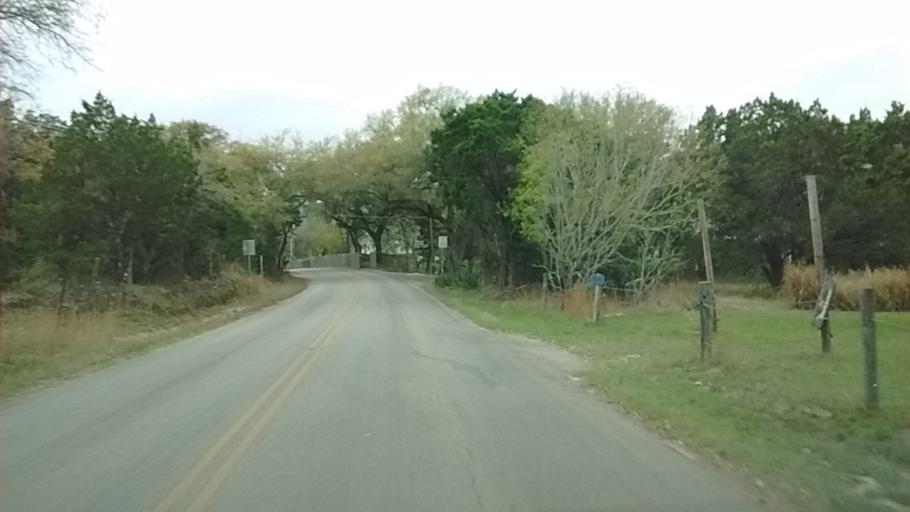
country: US
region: Texas
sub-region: Comal County
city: New Braunfels
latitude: 29.8045
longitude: -98.1607
